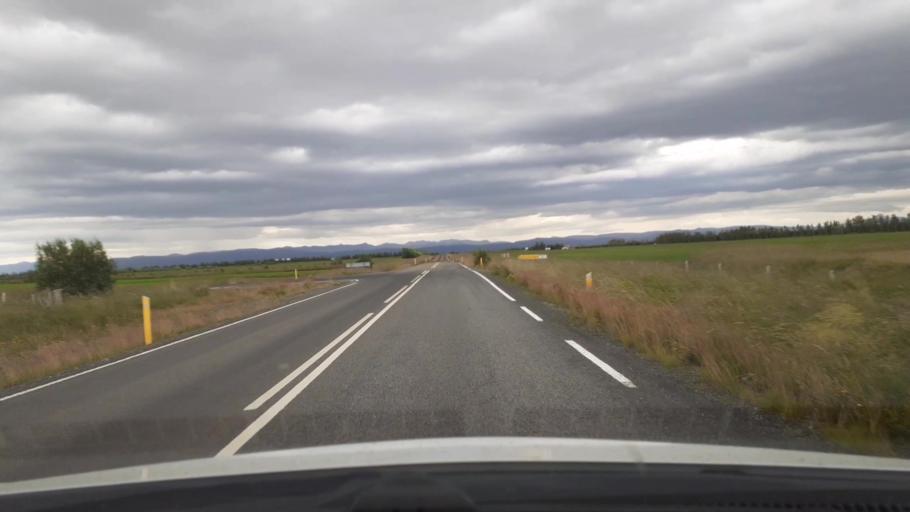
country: IS
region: West
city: Borgarnes
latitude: 64.5617
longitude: -21.7373
